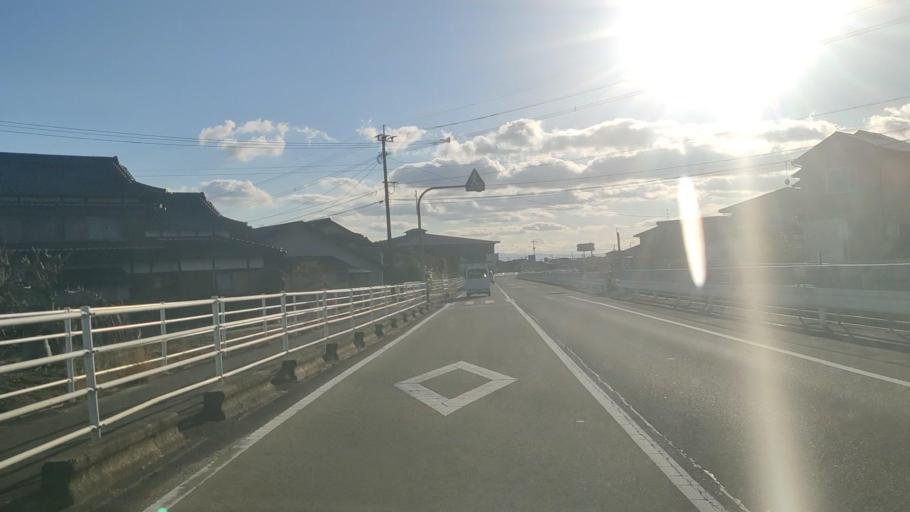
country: JP
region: Saga Prefecture
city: Saga-shi
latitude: 33.2759
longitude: 130.2225
